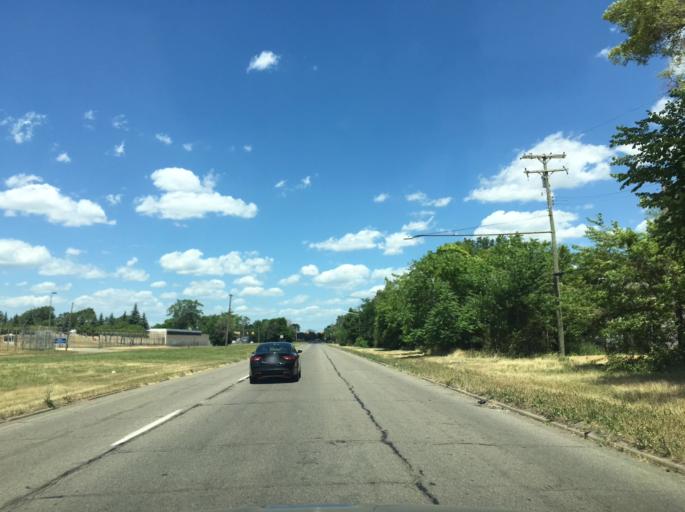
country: US
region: Michigan
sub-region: Wayne County
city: Hamtramck
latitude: 42.4236
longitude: -83.0429
